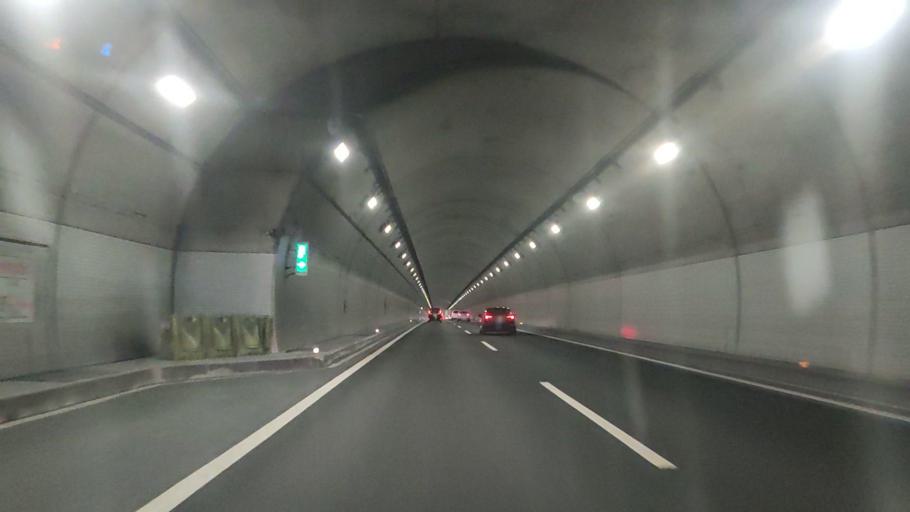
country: JP
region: Fukuoka
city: Kanda
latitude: 33.8093
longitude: 130.9143
